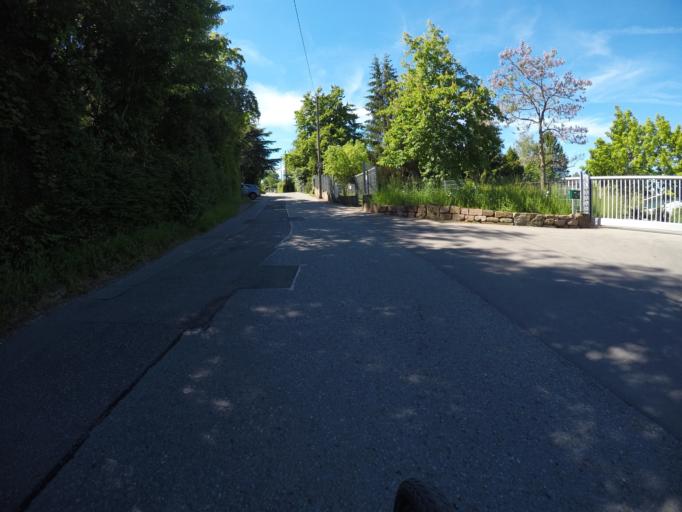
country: DE
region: Baden-Wuerttemberg
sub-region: Karlsruhe Region
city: Pforzheim
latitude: 48.9033
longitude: 8.6916
